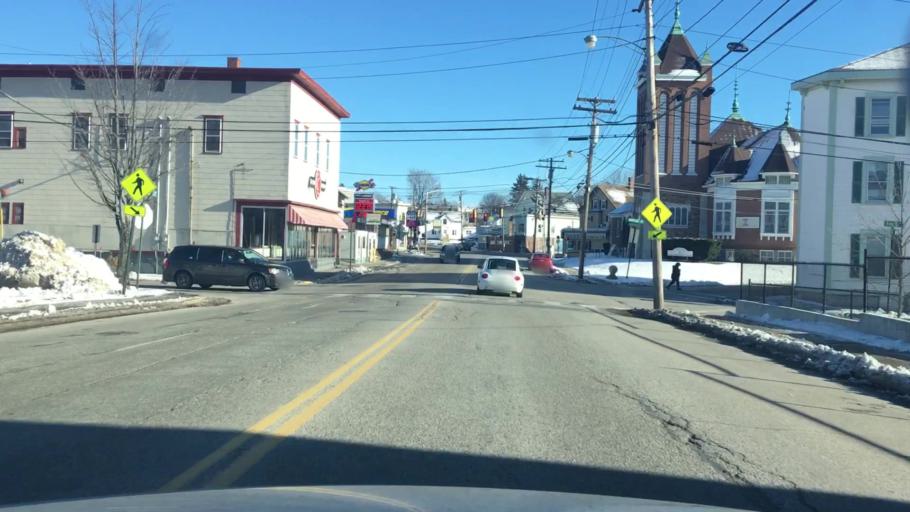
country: US
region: Maine
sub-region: Androscoggin County
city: Lewiston
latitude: 44.1003
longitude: -70.2137
